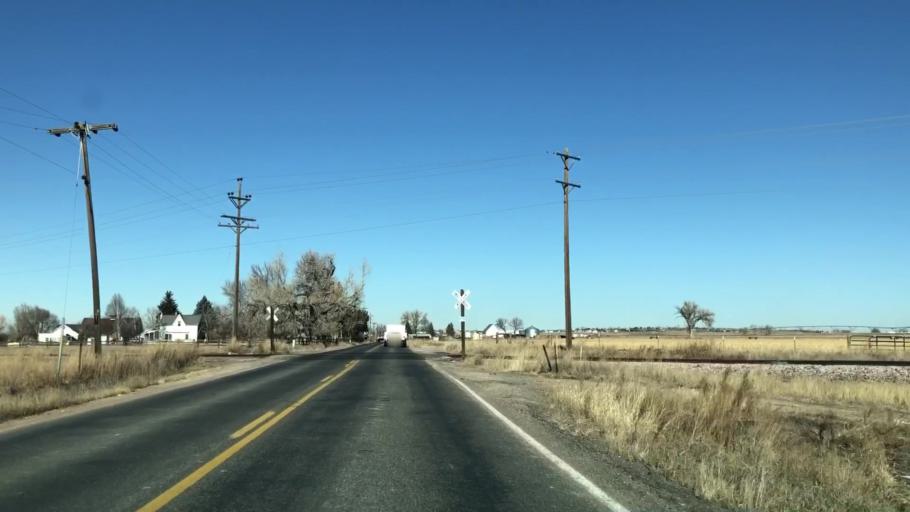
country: US
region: Colorado
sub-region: Weld County
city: Windsor
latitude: 40.5046
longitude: -104.9441
